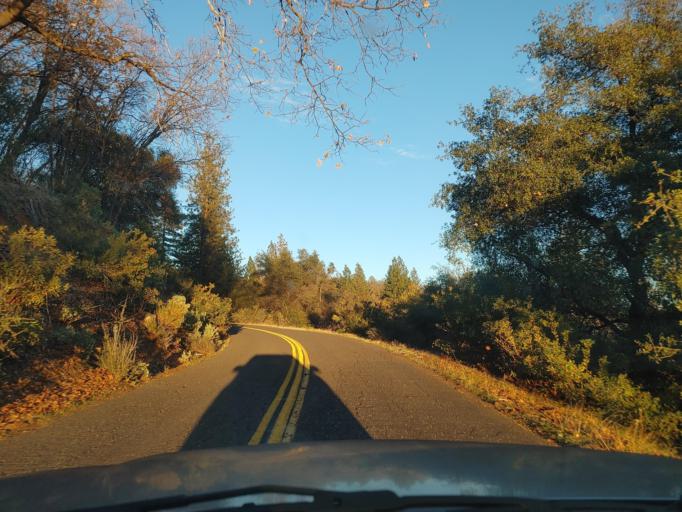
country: US
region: California
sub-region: Tuolumne County
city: Cedar Ridge
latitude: 38.0373
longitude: -120.3084
